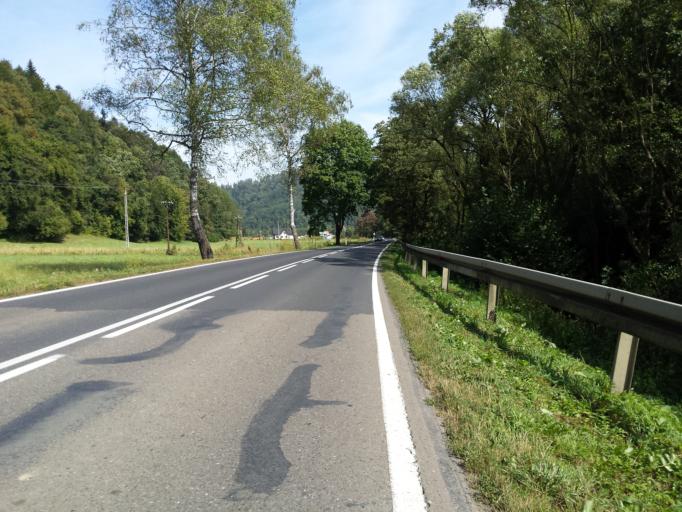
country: PL
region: Subcarpathian Voivodeship
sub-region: Powiat leski
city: Lesko
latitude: 49.4363
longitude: 22.3432
